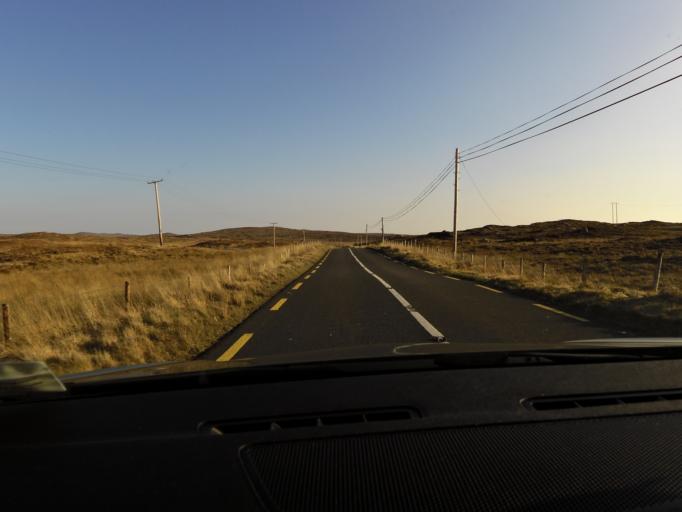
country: IE
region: Connaught
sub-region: County Galway
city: Oughterard
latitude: 53.3563
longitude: -9.5420
